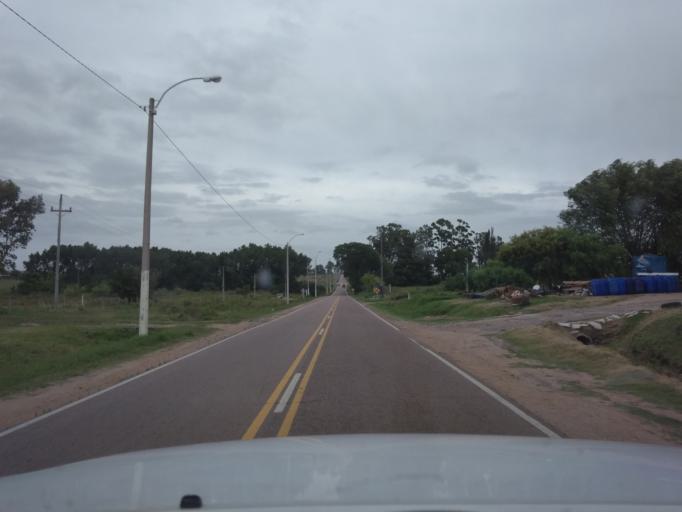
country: UY
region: Canelones
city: Tala
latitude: -34.3531
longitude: -55.7695
